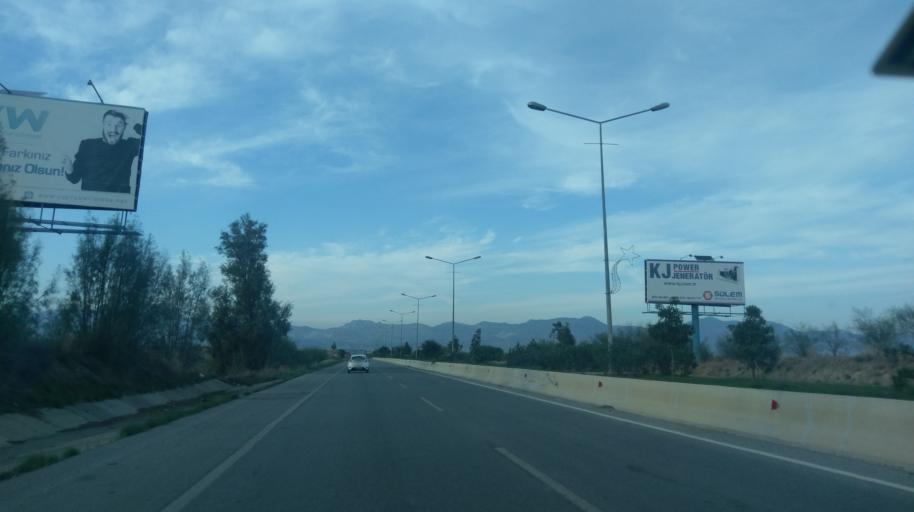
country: CY
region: Lefkosia
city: Geri
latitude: 35.1718
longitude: 33.5030
